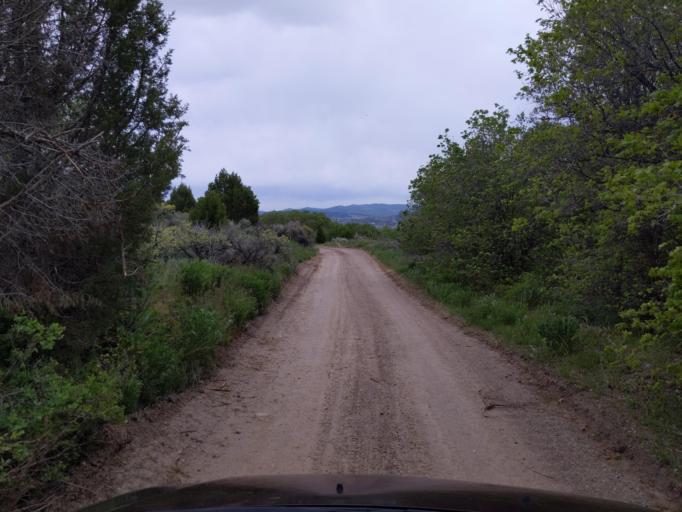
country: US
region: Idaho
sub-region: Bannock County
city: Pocatello
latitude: 42.8322
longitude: -112.4782
